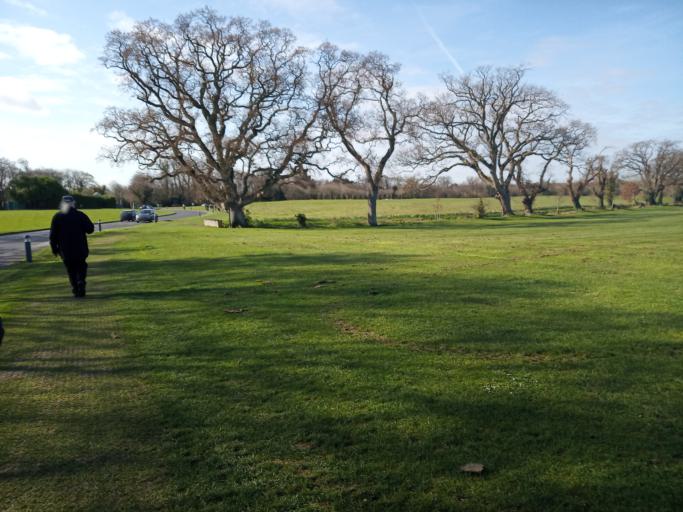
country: IE
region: Leinster
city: Malahide
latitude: 53.4420
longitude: -6.1640
